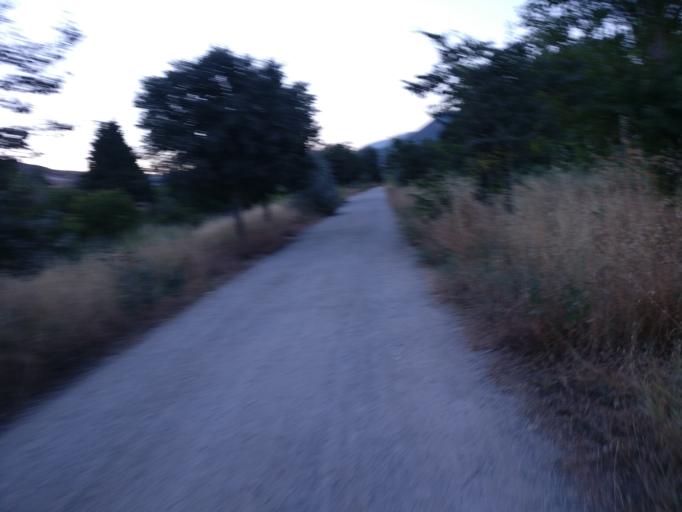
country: ES
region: Andalusia
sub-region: Provincia de Granada
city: Huetor Vega
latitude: 37.1614
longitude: -3.5622
